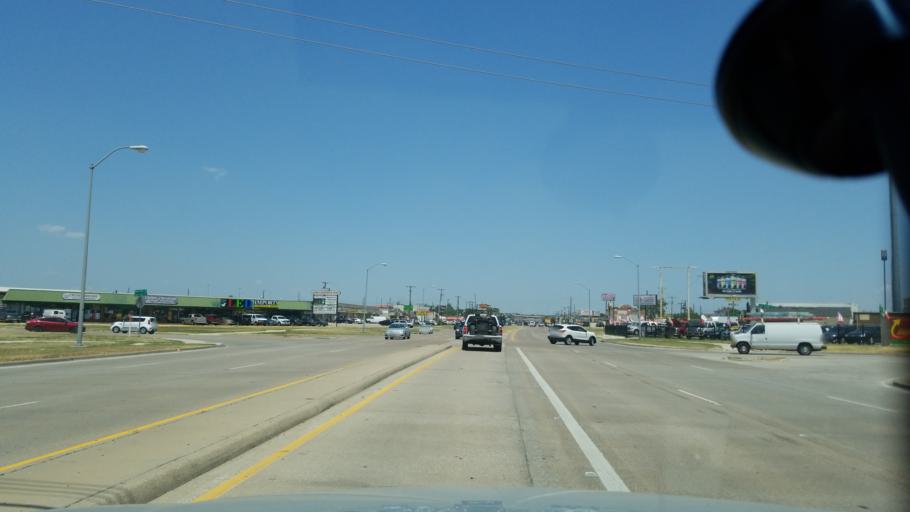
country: US
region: Texas
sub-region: Dallas County
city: Farmers Branch
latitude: 32.8924
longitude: -96.8903
